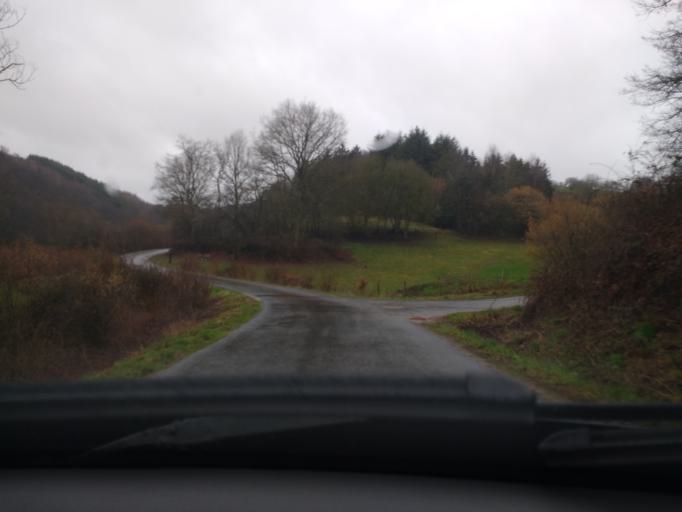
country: DE
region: Rheinland-Pfalz
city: Franzenheim
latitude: 49.6925
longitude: 6.6842
